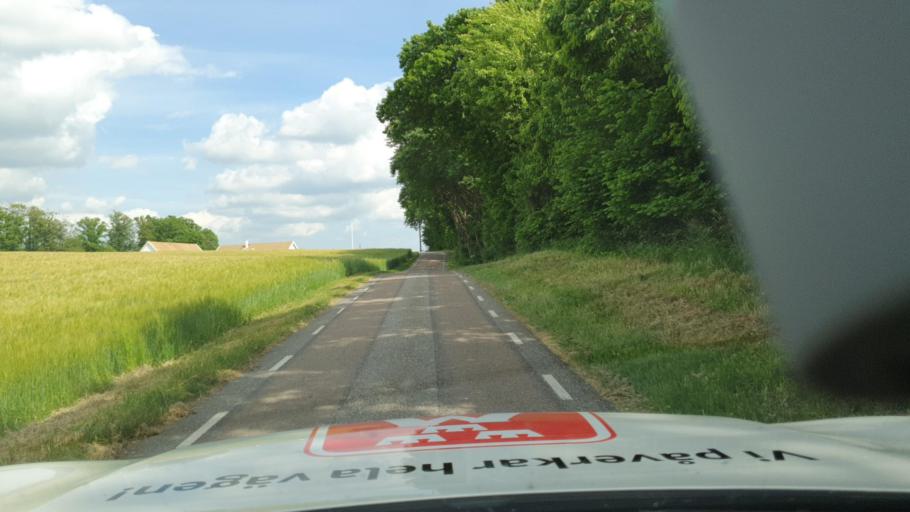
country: SE
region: Skane
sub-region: Skurups Kommun
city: Skurup
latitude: 55.5240
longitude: 13.4460
